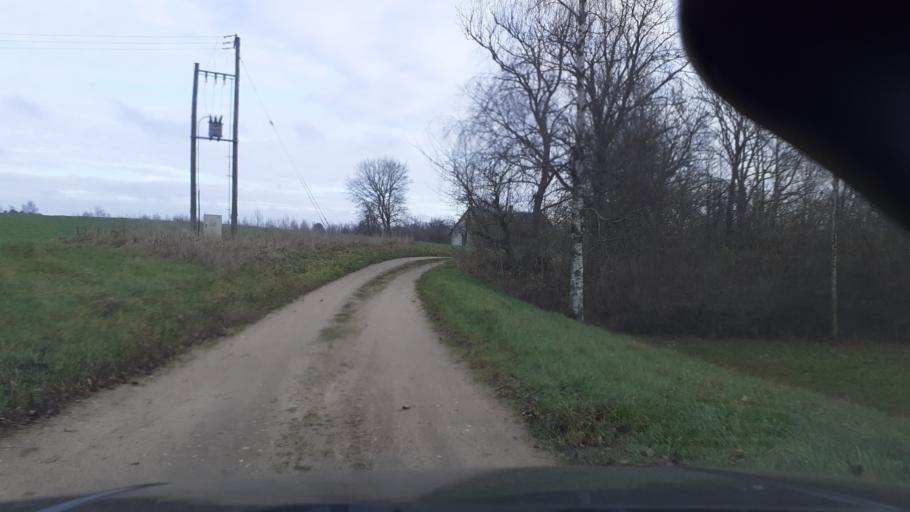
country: LV
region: Alsunga
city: Alsunga
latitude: 56.9442
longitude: 21.6398
